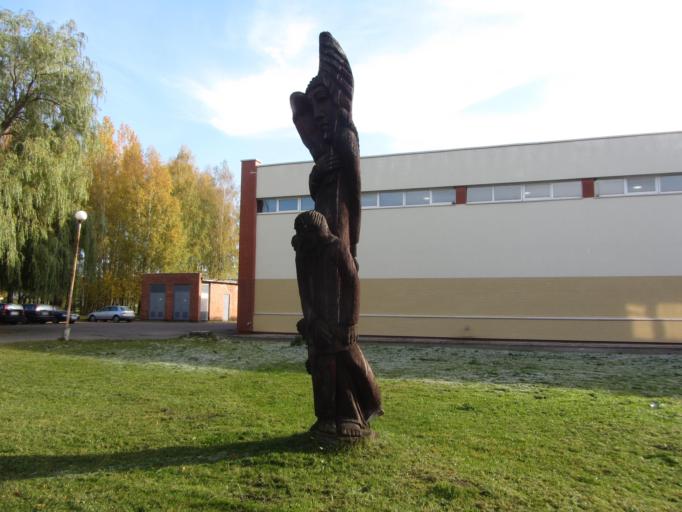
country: LT
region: Vilnius County
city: Elektrenai
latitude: 54.7815
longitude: 24.6542
